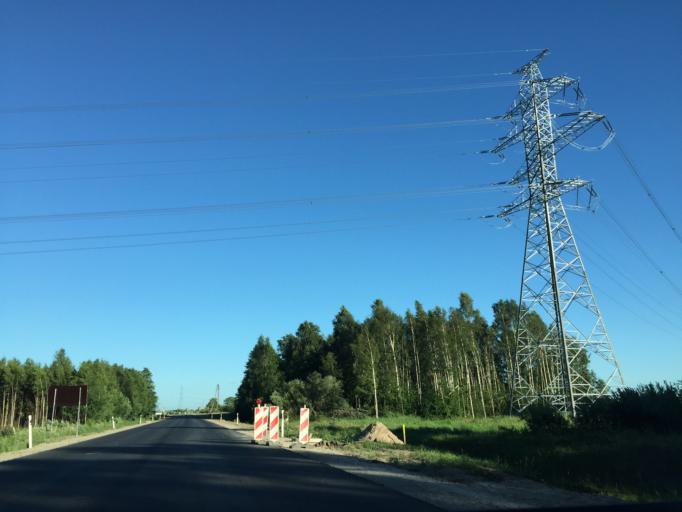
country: LV
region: Ventspils
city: Ventspils
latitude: 57.3963
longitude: 21.6339
